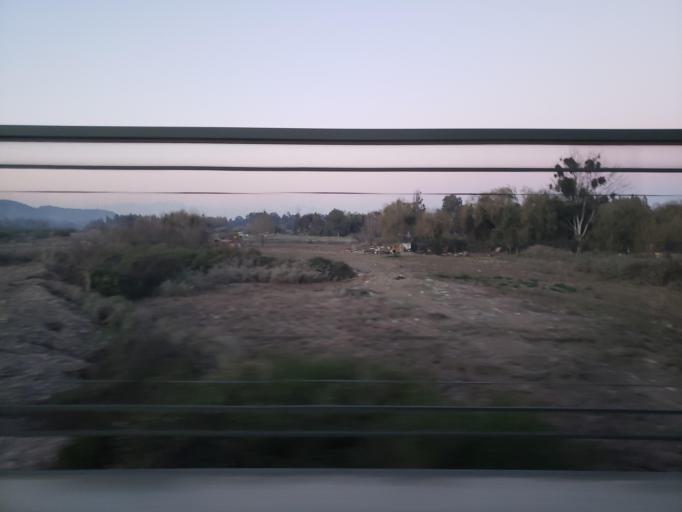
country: CL
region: Santiago Metropolitan
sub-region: Provincia de Talagante
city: El Monte
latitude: -33.6840
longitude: -70.9755
